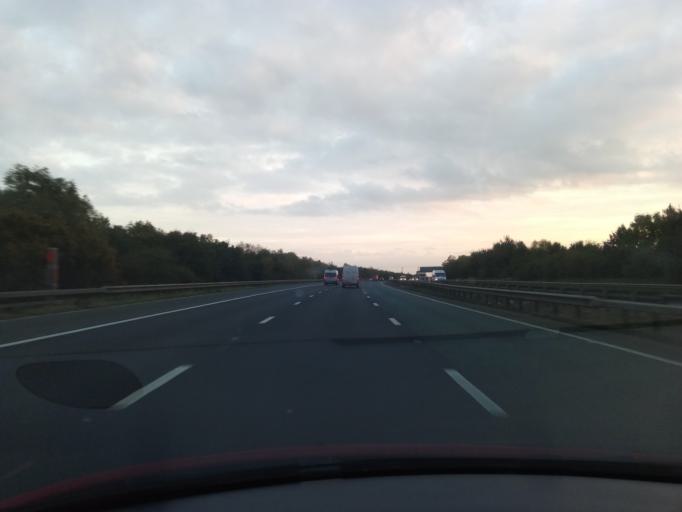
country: GB
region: England
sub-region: City and Borough of Leeds
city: Wetherby
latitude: 54.0021
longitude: -1.3695
